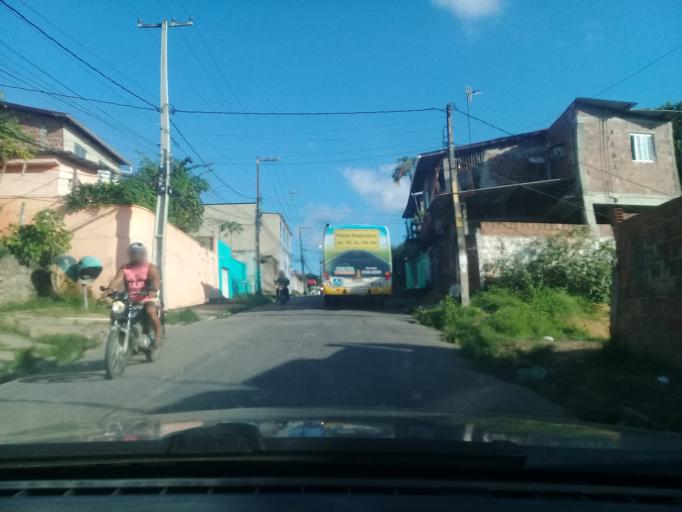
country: BR
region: Pernambuco
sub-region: Jaboatao Dos Guararapes
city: Jaboatao dos Guararapes
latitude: -8.1042
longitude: -34.9641
